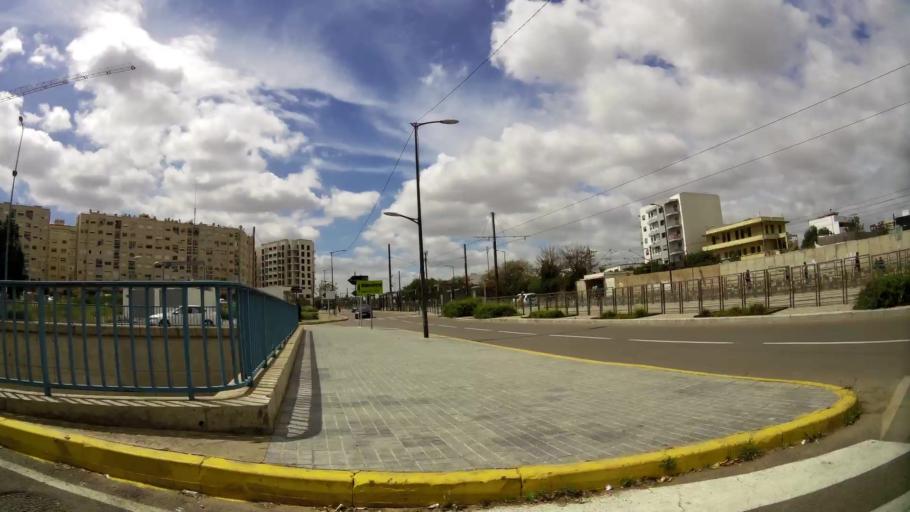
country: MA
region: Grand Casablanca
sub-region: Casablanca
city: Casablanca
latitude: 33.5557
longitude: -7.6306
